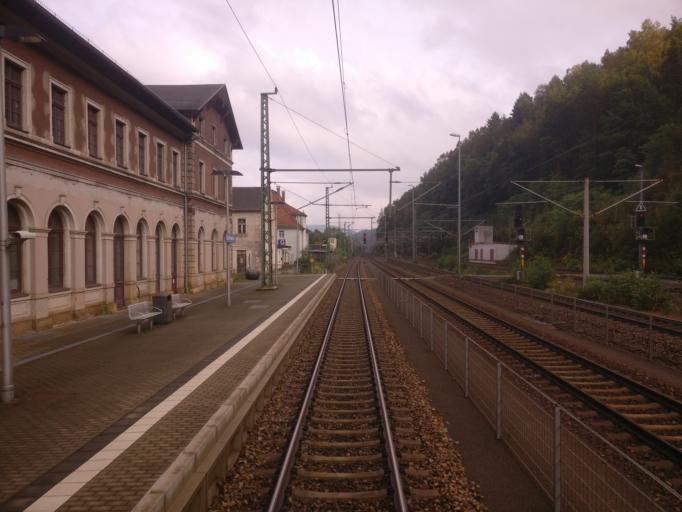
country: DE
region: Saxony
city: Rathmannsdorf
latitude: 50.9187
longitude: 14.1400
